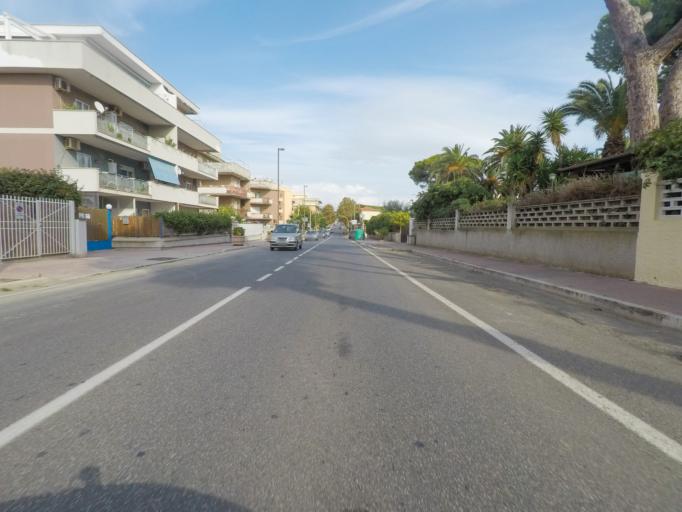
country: IT
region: Latium
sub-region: Citta metropolitana di Roma Capitale
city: Santa Marinella
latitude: 42.0322
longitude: 11.8458
